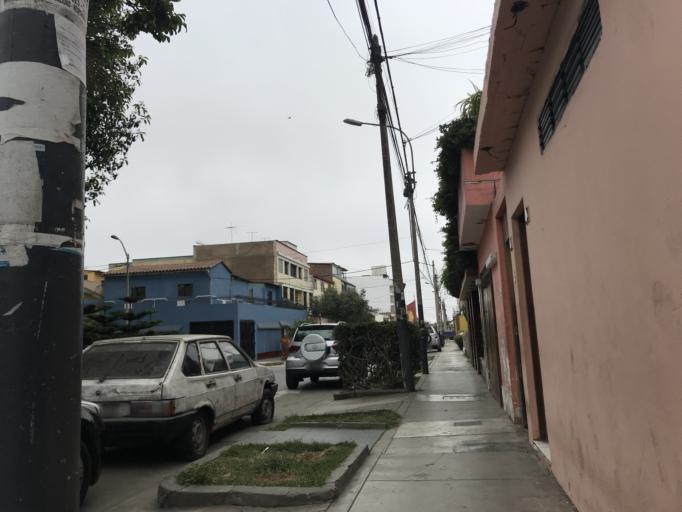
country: PE
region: Lima
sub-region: Lima
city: San Isidro
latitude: -12.0789
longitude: -77.0690
